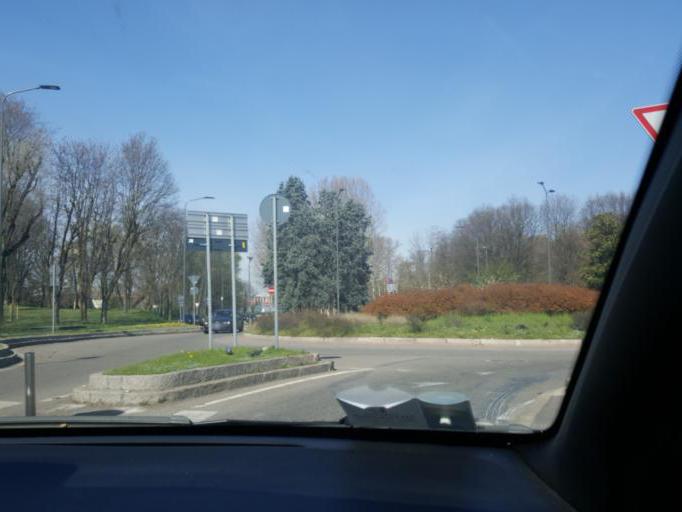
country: IT
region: Lombardy
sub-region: Citta metropolitana di Milano
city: Novate Milanese
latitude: 45.4859
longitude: 9.1375
